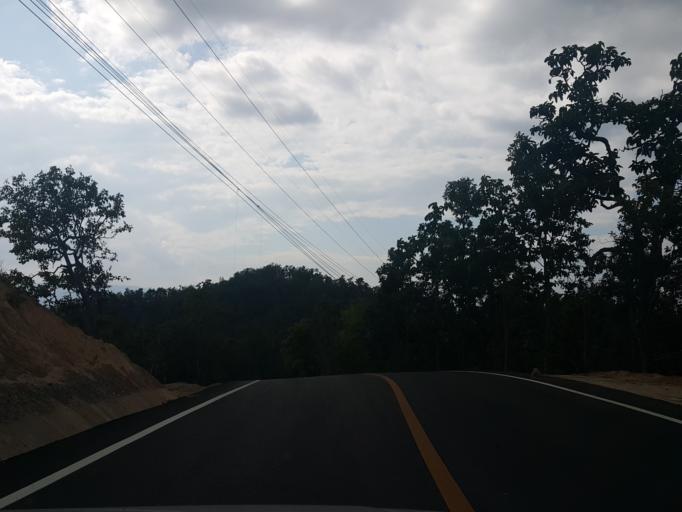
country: TH
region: Chiang Mai
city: Mae Chaem
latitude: 18.5097
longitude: 98.4295
